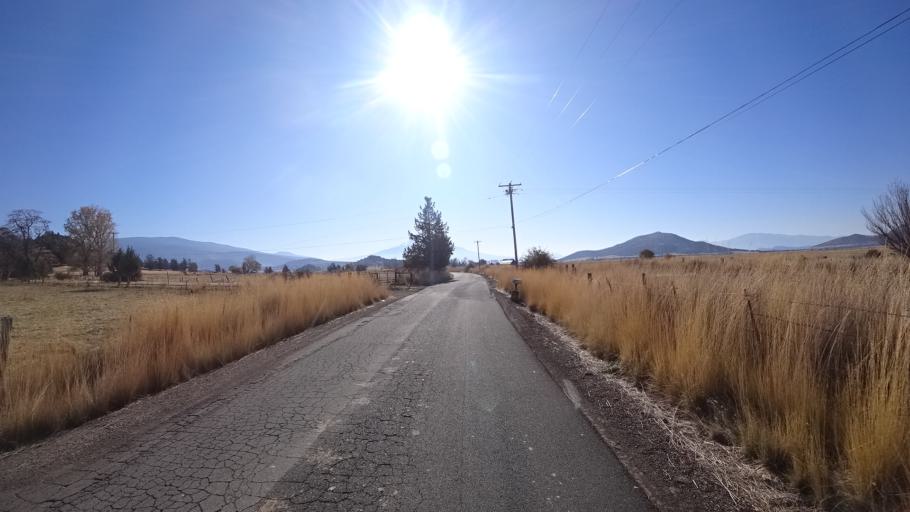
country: US
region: California
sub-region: Siskiyou County
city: Montague
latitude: 41.7042
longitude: -122.3787
